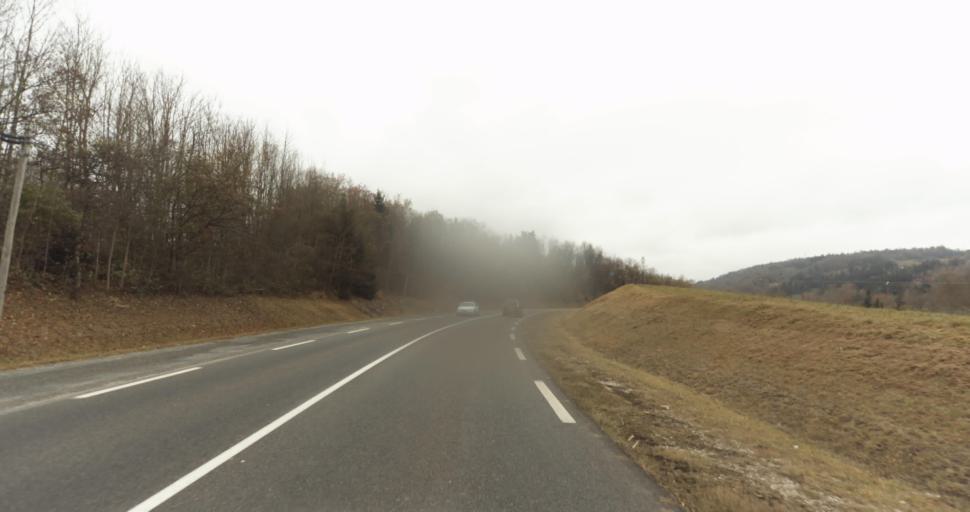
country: FR
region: Rhone-Alpes
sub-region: Departement de la Haute-Savoie
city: Evires
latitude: 46.0394
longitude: 6.2467
